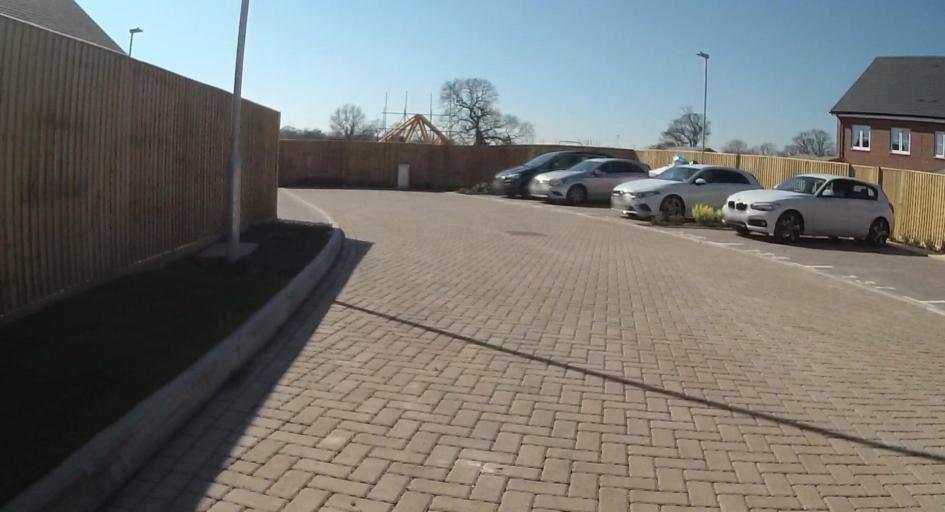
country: GB
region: England
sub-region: Wokingham
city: Wokingham
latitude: 51.4232
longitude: -0.8255
